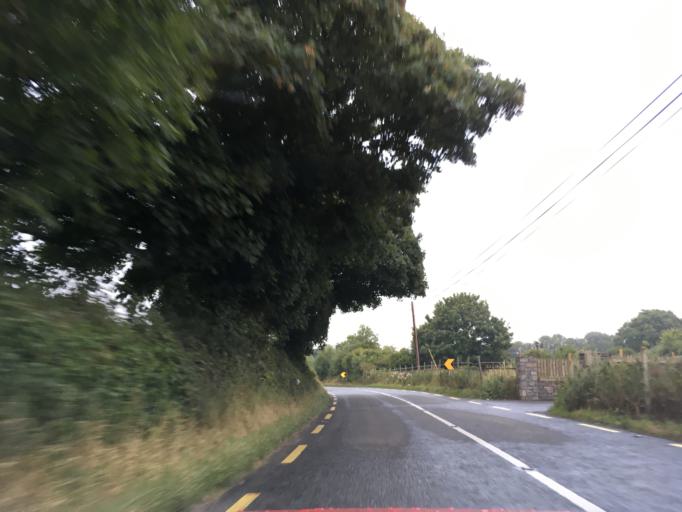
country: IE
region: Munster
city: Tipperary
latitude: 52.4896
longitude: -8.0452
